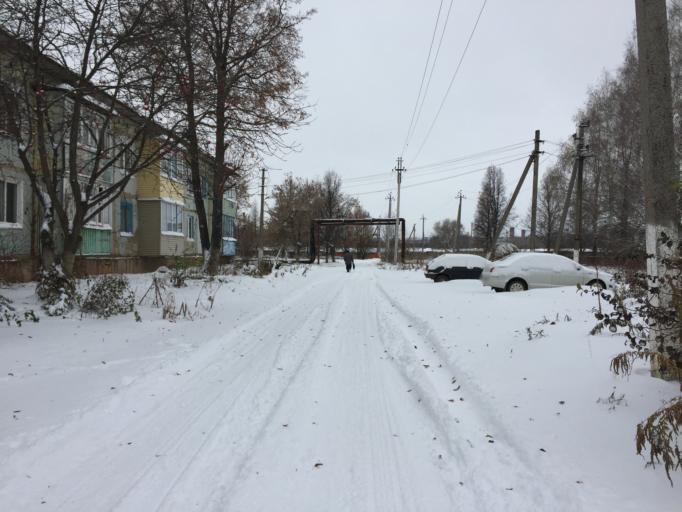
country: RU
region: Tula
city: Shchekino
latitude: 53.8523
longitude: 37.4798
